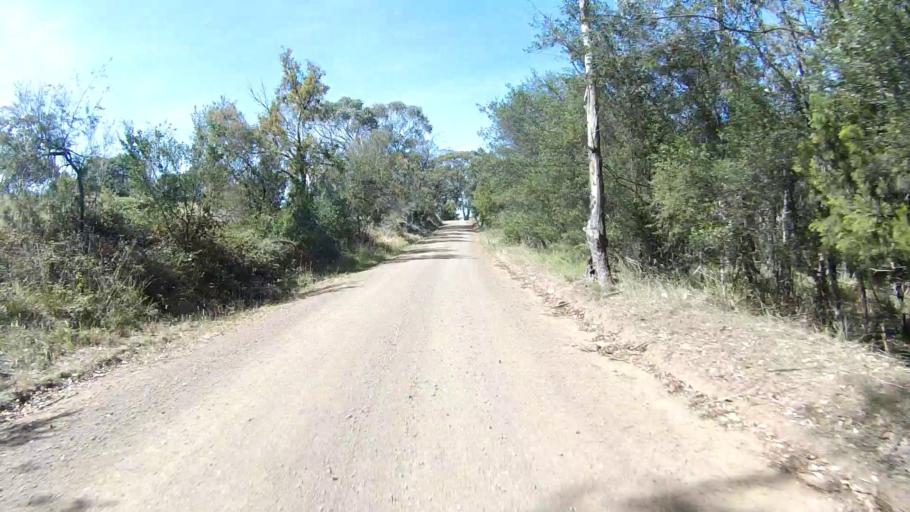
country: AU
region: Tasmania
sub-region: Sorell
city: Sorell
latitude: -42.7187
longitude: 147.5956
